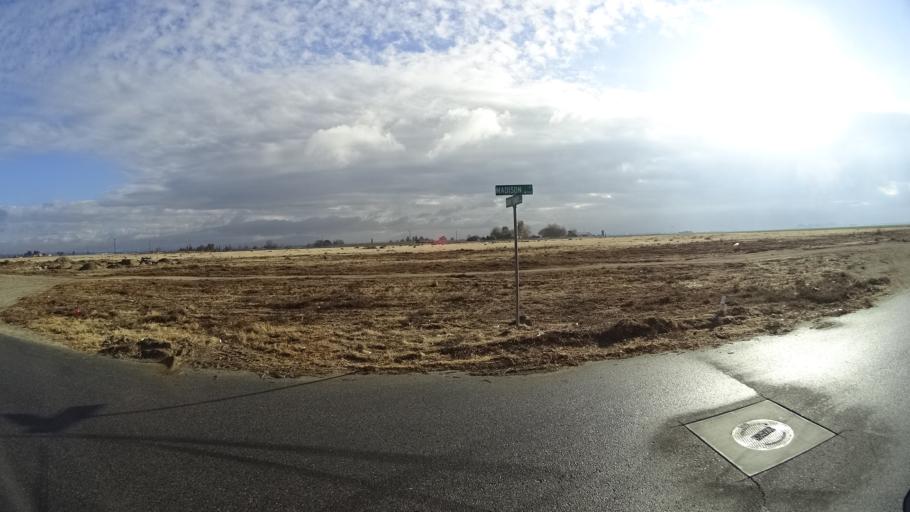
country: US
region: California
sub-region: Kern County
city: Greenfield
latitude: 35.2900
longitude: -118.9942
